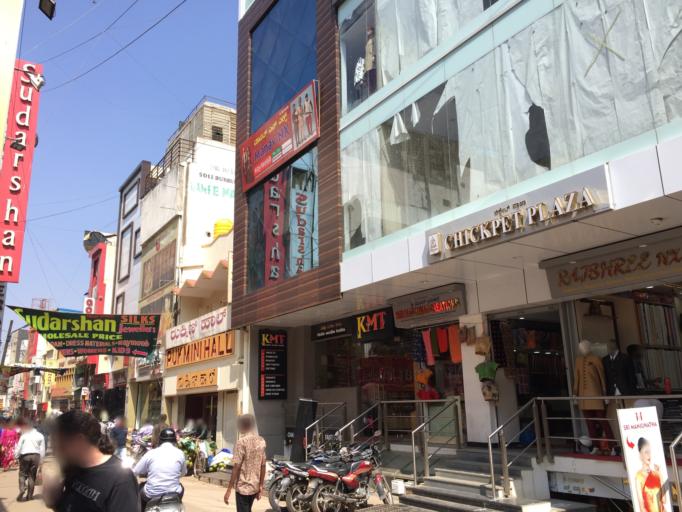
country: IN
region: Karnataka
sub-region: Bangalore Urban
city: Bangalore
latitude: 12.9690
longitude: 77.5770
